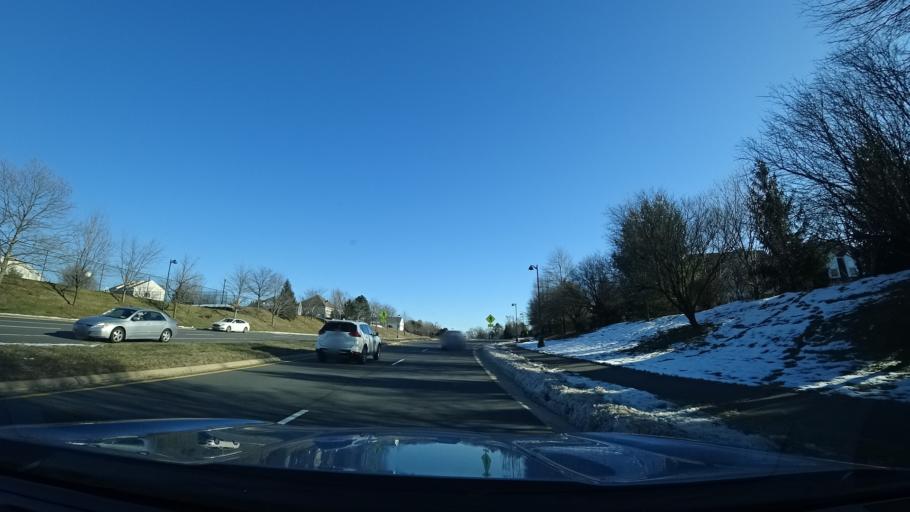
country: US
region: Virginia
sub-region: Loudoun County
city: Ashburn
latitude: 39.0533
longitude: -77.4881
